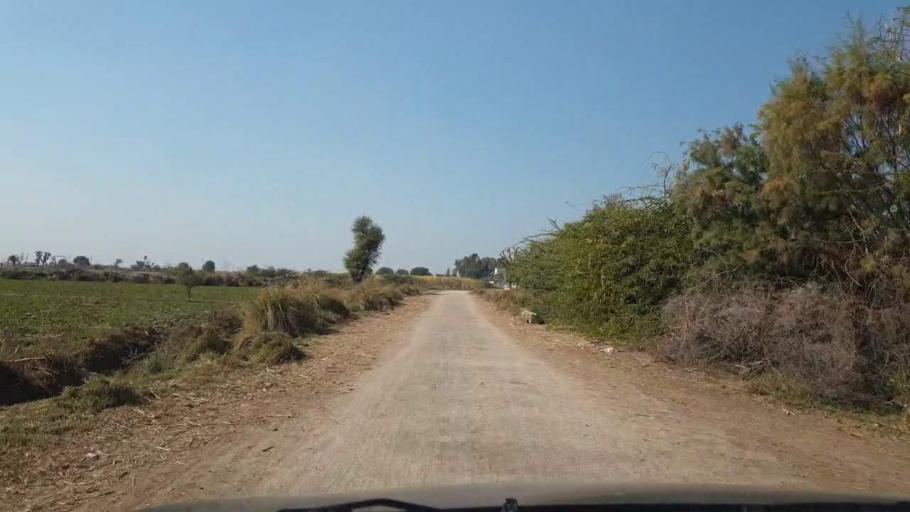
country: PK
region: Sindh
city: Jhol
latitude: 25.9133
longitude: 68.8134
